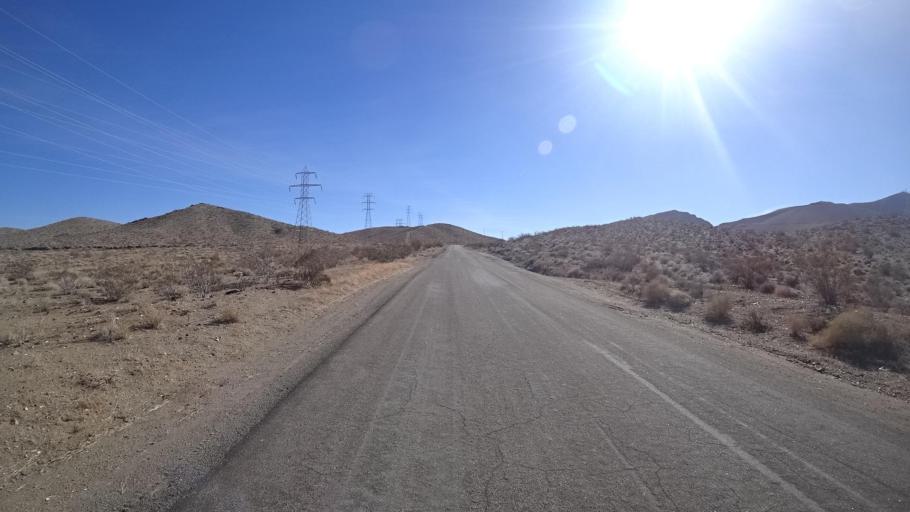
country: US
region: California
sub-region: Kern County
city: Ridgecrest
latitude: 35.3772
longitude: -117.6569
